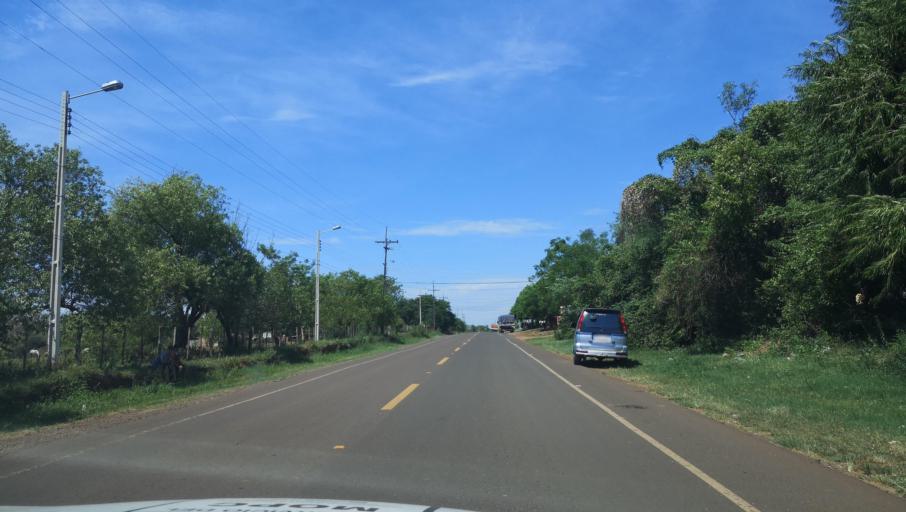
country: PY
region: Misiones
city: Santa Maria
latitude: -26.9008
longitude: -57.0281
